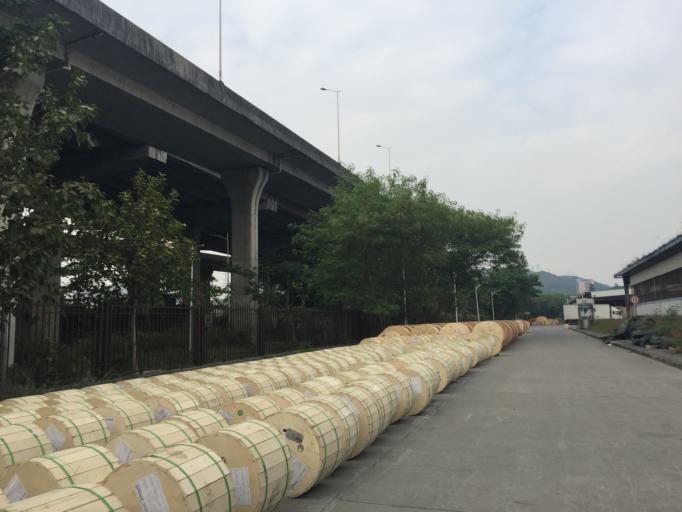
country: CN
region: Guangdong
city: Xin'an
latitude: 22.5802
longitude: 113.9256
